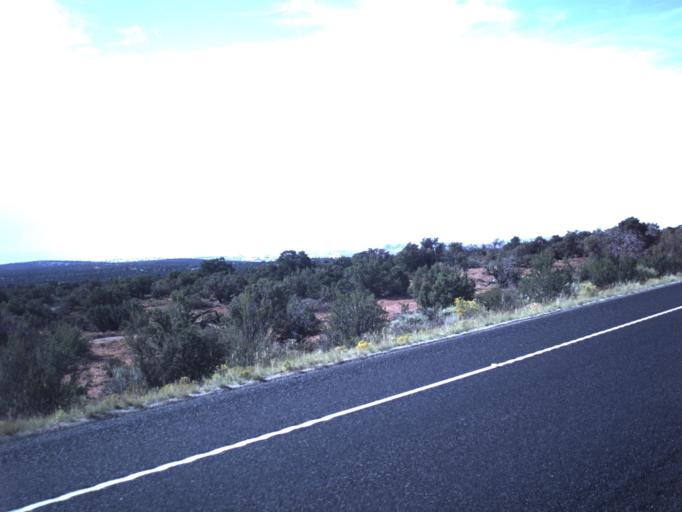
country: US
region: Utah
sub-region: Grand County
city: Moab
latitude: 38.5693
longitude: -109.7917
